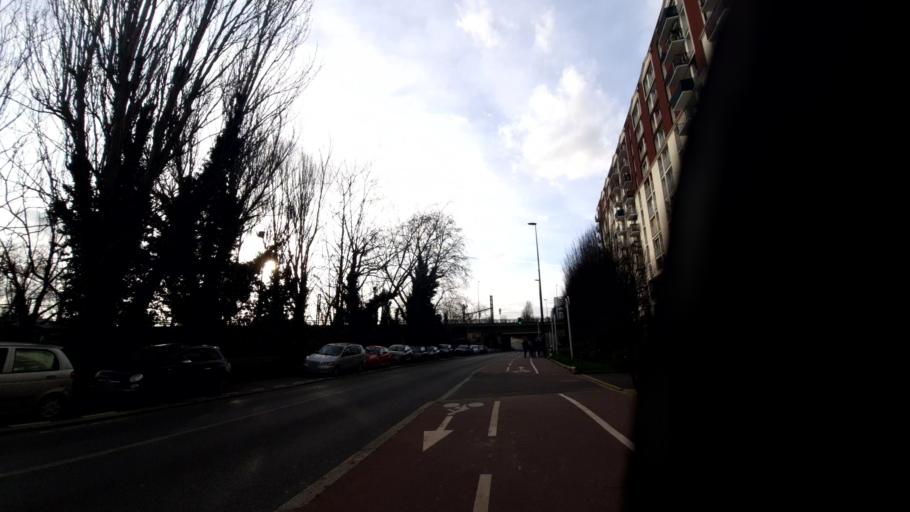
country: FR
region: Ile-de-France
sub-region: Departement du Val-de-Marne
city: Charenton-le-Pont
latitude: 48.8180
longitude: 2.4164
